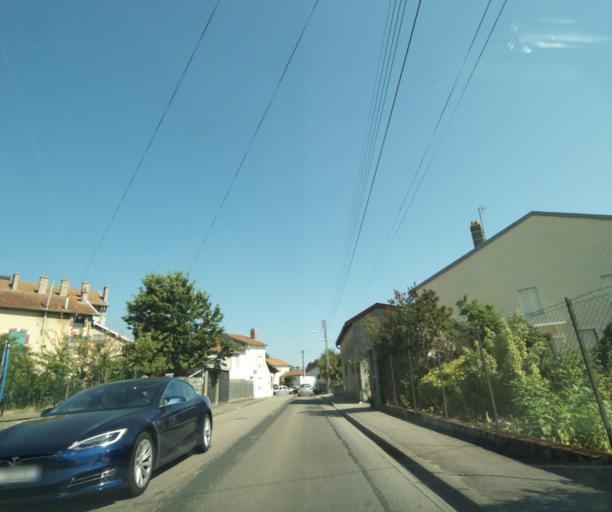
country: FR
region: Lorraine
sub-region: Departement de Meurthe-et-Moselle
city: Toul
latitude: 48.6677
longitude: 5.8828
